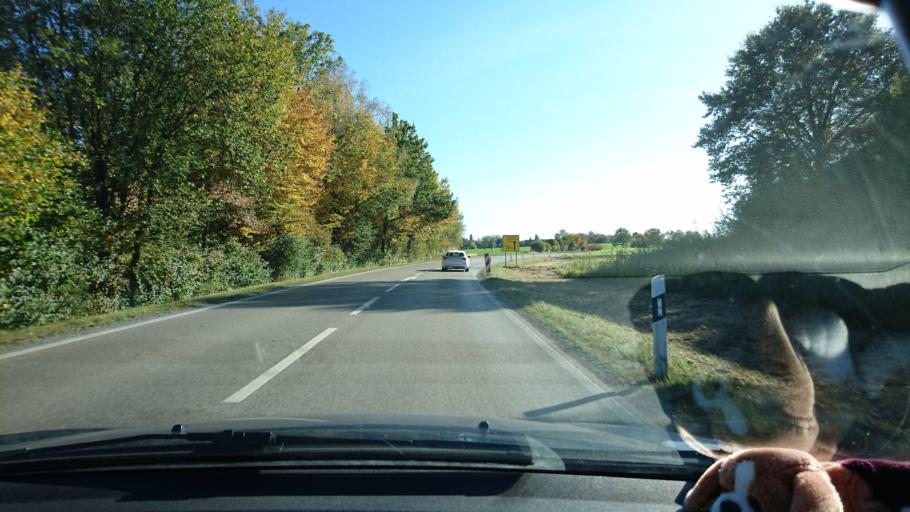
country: DE
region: Bavaria
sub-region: Upper Bavaria
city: Zorneding
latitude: 48.1042
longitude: 11.8305
